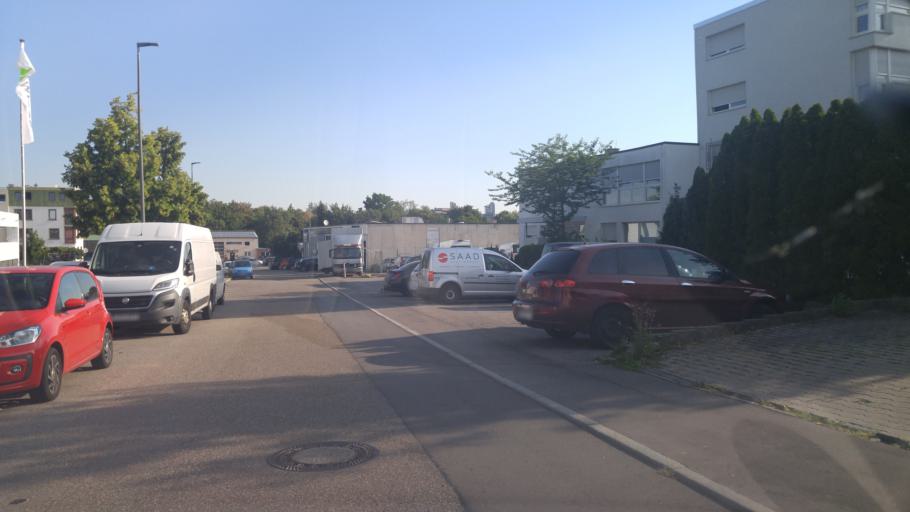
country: DE
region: Baden-Wuerttemberg
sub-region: Regierungsbezirk Stuttgart
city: Leonberg
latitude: 48.7855
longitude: 9.0017
